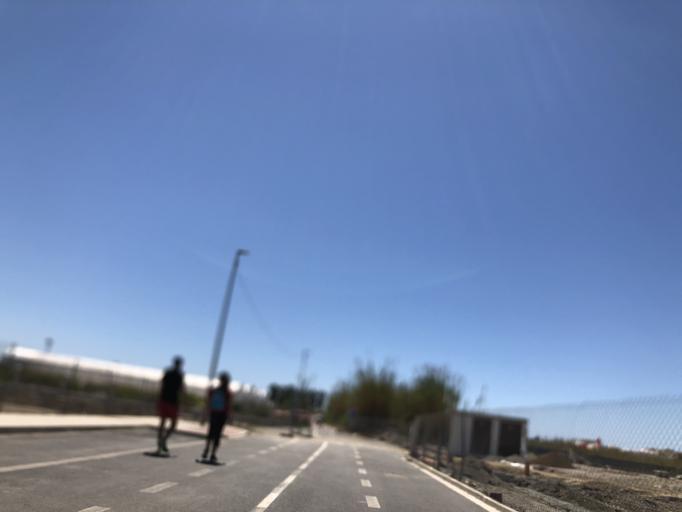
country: ES
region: Andalusia
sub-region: Provincia de Almeria
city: Almeria
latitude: 36.8361
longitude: -2.4044
